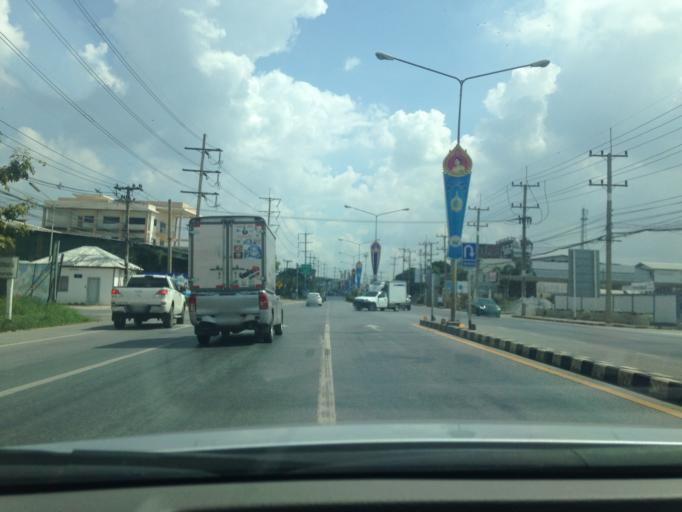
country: TH
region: Pathum Thani
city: Sam Khok
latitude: 14.0712
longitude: 100.5218
